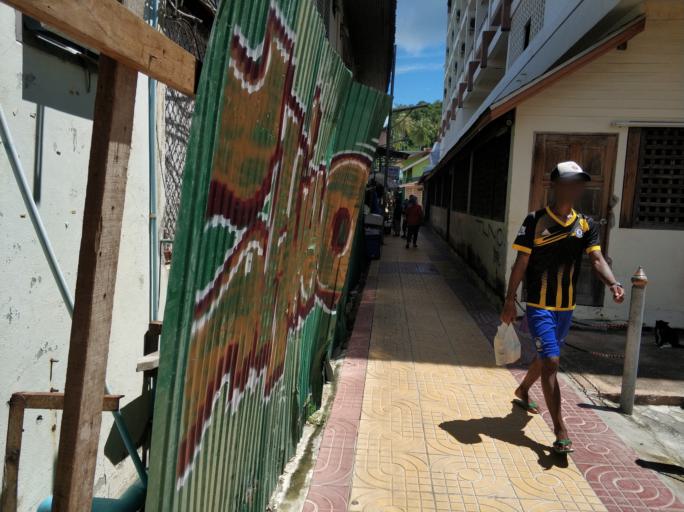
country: TH
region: Phangnga
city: Ban Phru Nai
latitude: 7.7394
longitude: 98.7710
